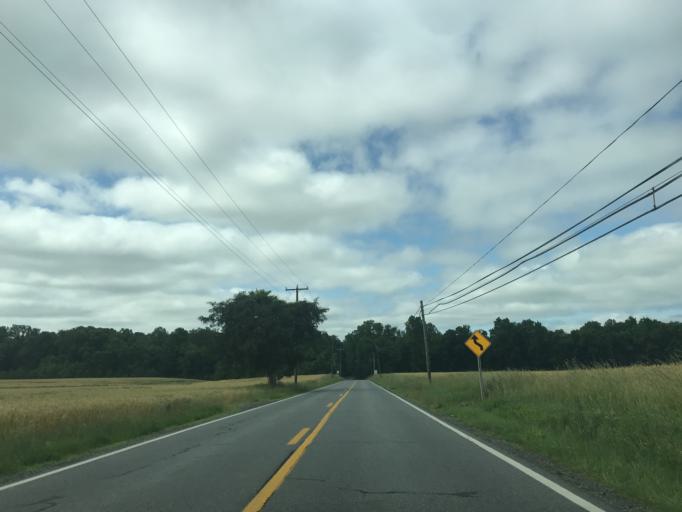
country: US
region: Maryland
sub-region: Caroline County
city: Ridgely
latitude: 38.8952
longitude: -75.9597
